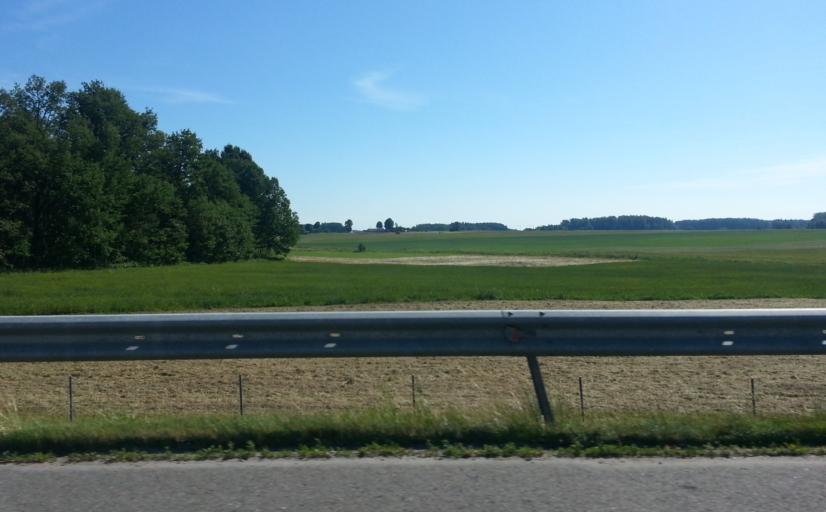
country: LT
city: Sirvintos
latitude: 55.0294
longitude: 24.9023
